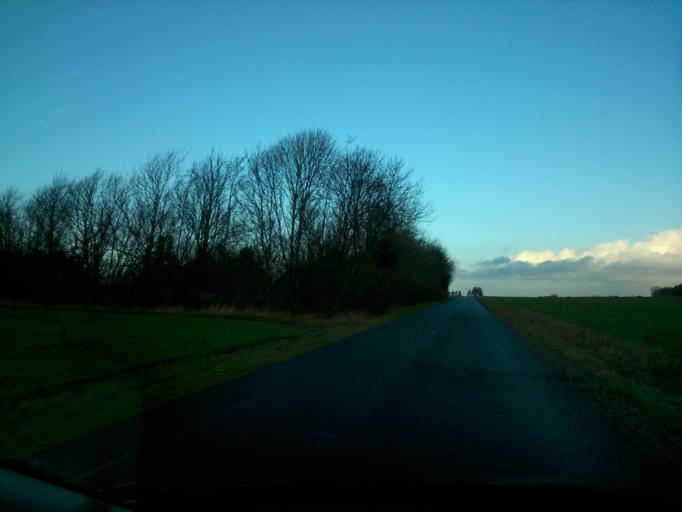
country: DK
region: Central Jutland
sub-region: Ringkobing-Skjern Kommune
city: Videbaek
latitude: 56.0402
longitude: 8.5662
